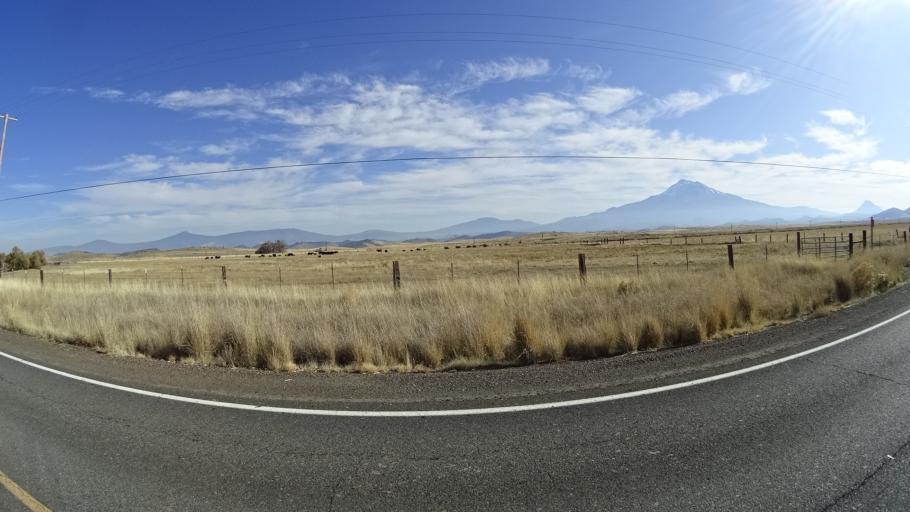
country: US
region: California
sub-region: Siskiyou County
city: Weed
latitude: 41.5079
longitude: -122.5171
